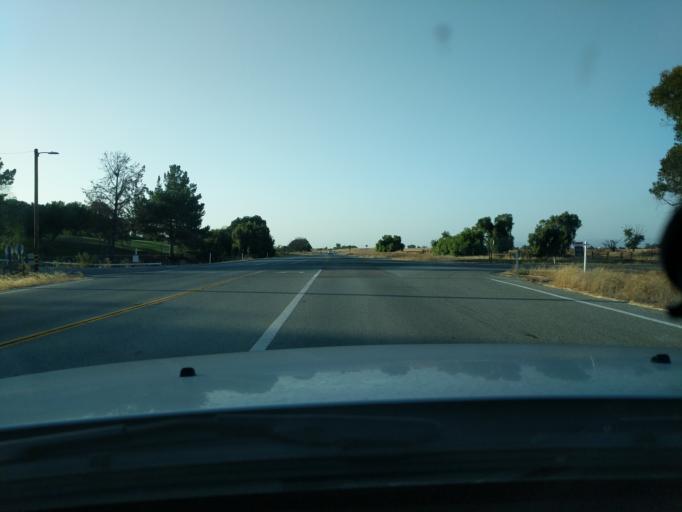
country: US
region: California
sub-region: San Benito County
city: Ridgemark
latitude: 36.8089
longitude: -121.3455
